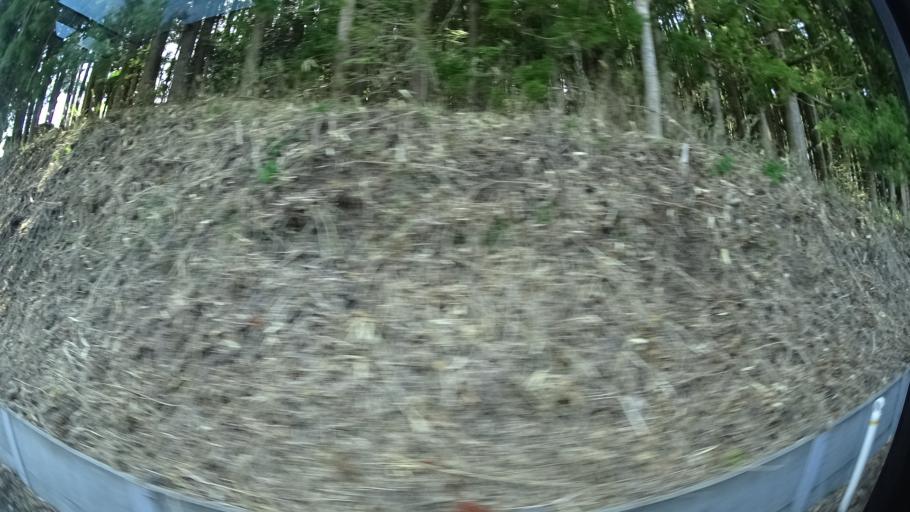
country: JP
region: Iwate
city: Ofunato
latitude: 38.9966
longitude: 141.7100
